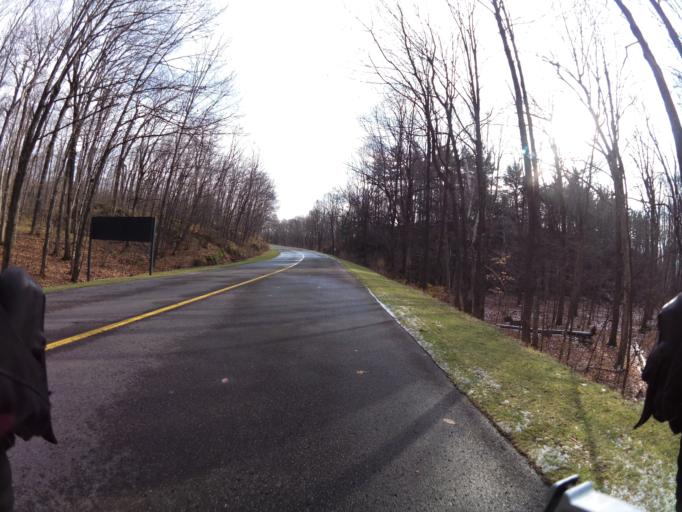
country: CA
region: Quebec
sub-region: Outaouais
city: Gatineau
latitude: 45.4704
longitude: -75.8276
